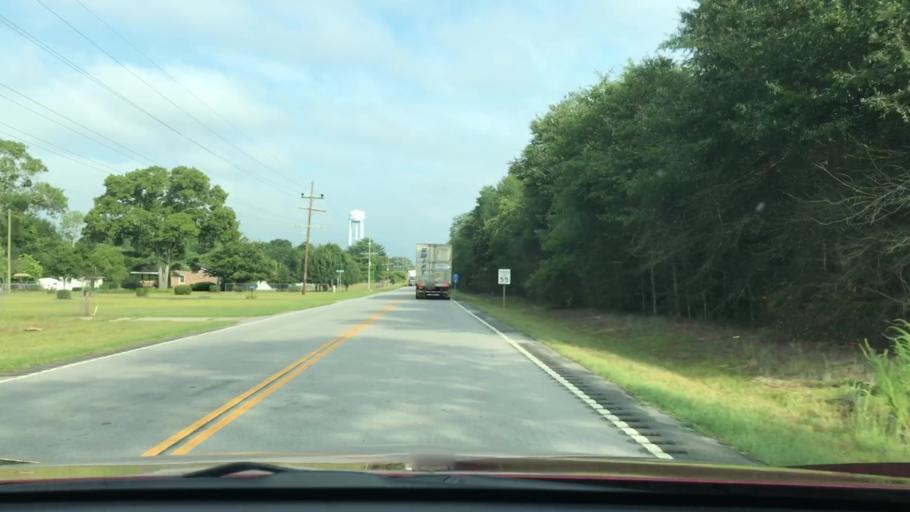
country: US
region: South Carolina
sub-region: Barnwell County
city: Williston
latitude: 33.6369
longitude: -81.3244
